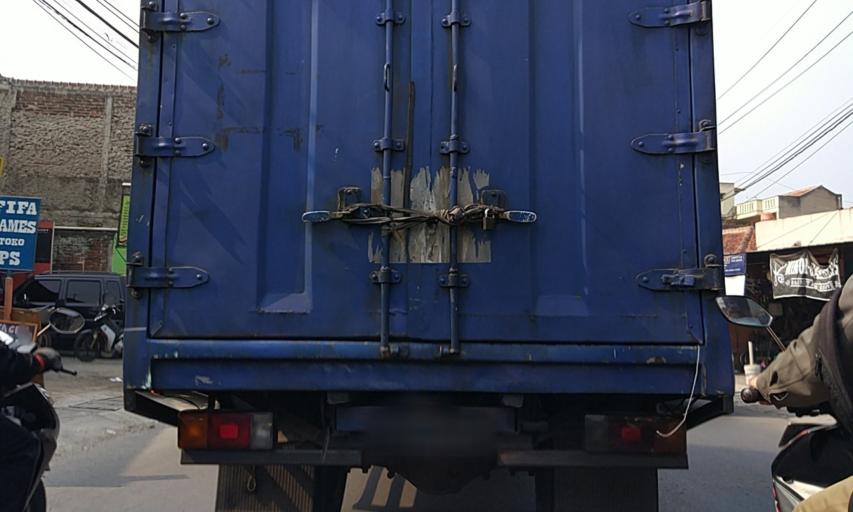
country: ID
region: West Java
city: Margahayukencana
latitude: -6.9858
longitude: 107.5606
